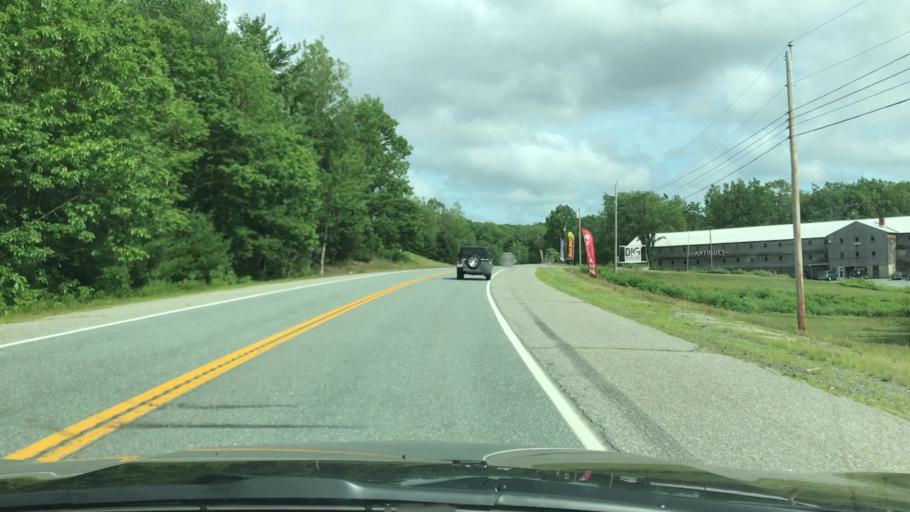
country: US
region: Maine
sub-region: Hancock County
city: Surry
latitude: 44.5629
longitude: -68.5883
